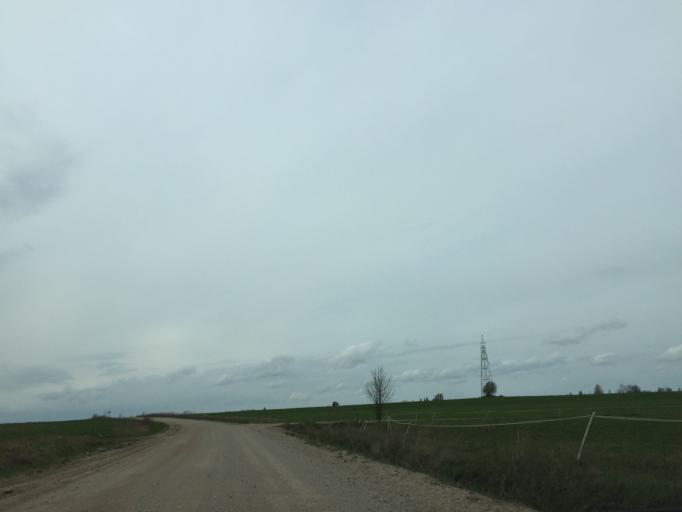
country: LV
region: Priekuli
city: Priekuli
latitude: 57.3412
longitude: 25.3590
